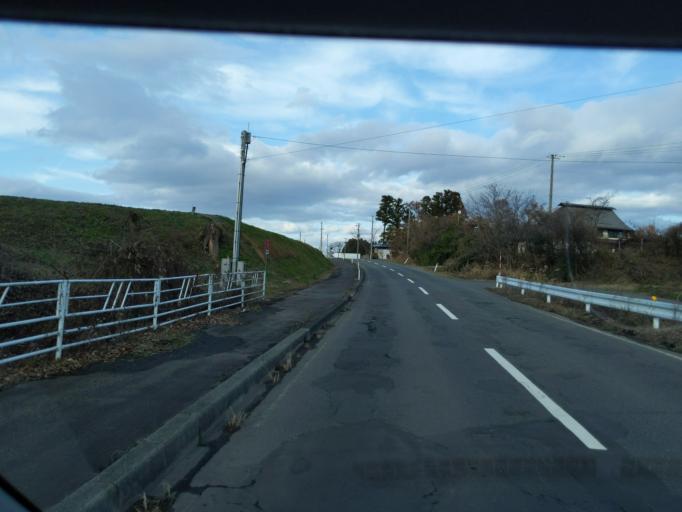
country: JP
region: Iwate
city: Mizusawa
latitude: 39.1841
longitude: 141.1055
